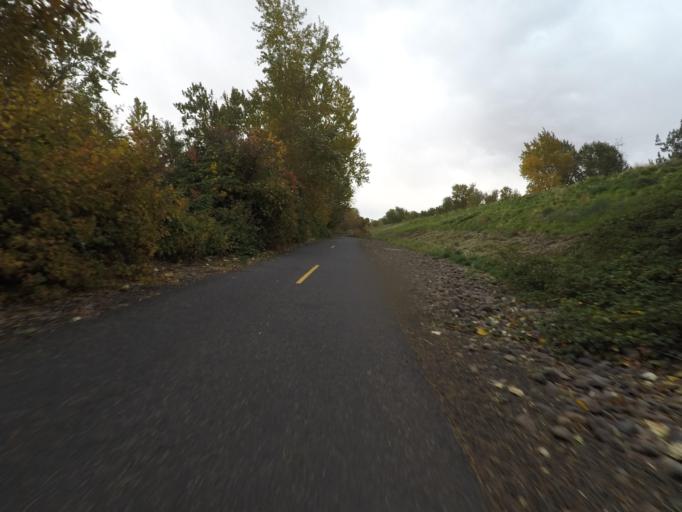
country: US
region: Washington
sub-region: Walla Walla County
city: Walla Walla East
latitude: 46.0815
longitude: -118.2539
